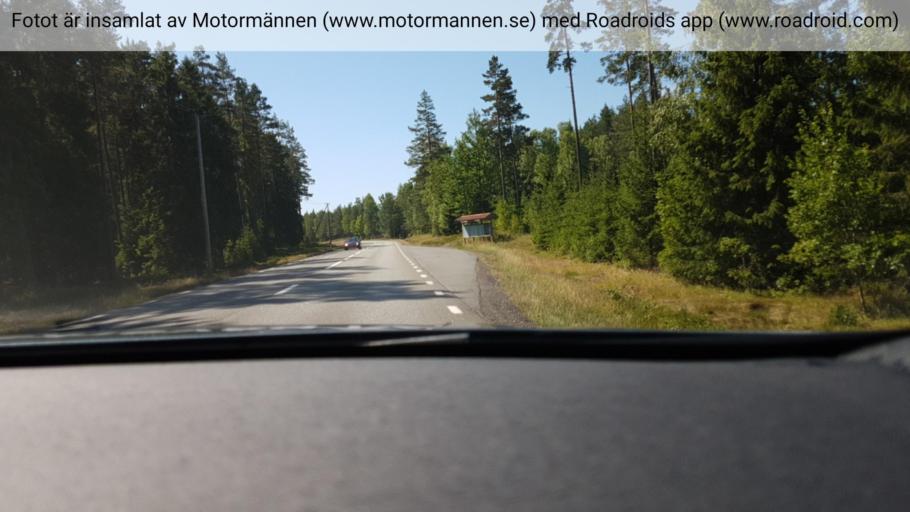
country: SE
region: Joenkoeping
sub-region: Mullsjo Kommun
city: Mullsjoe
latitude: 57.7827
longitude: 13.8348
